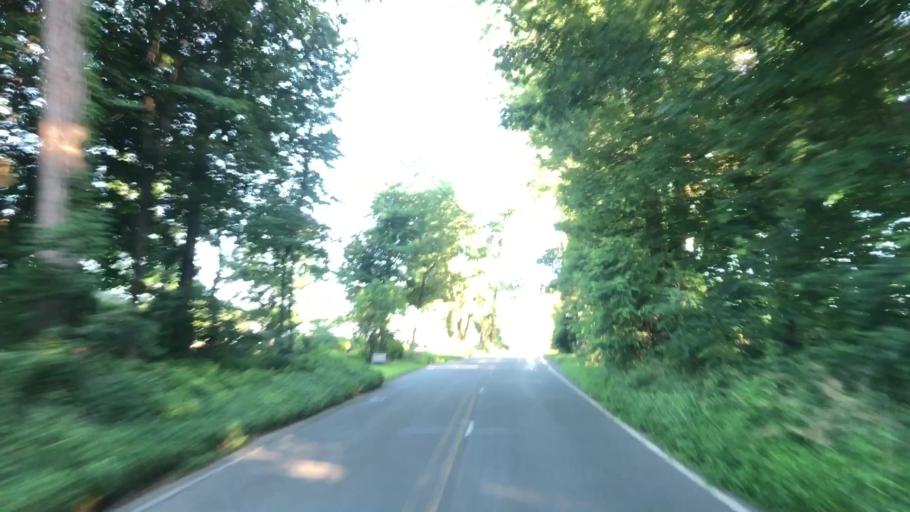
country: US
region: Massachusetts
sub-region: Hampshire County
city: Southampton
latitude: 42.2395
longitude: -72.7106
